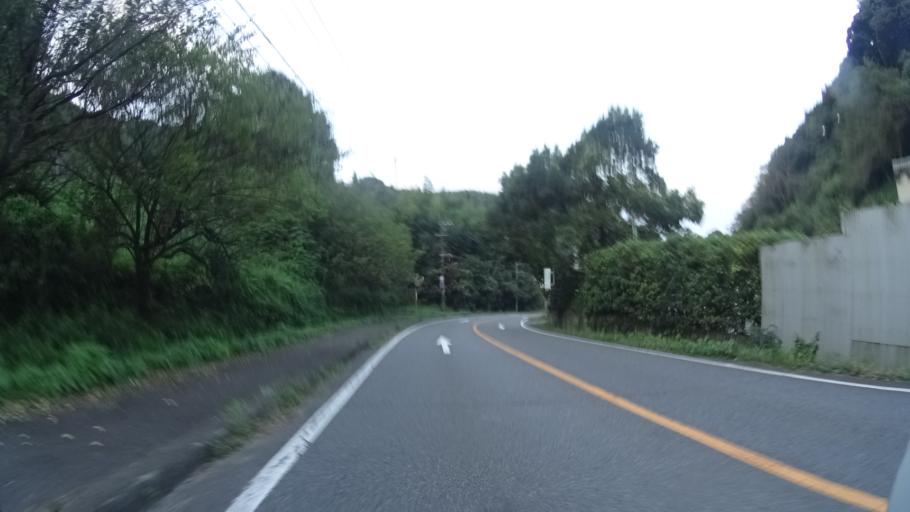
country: JP
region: Oita
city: Beppu
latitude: 33.3279
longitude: 131.4756
